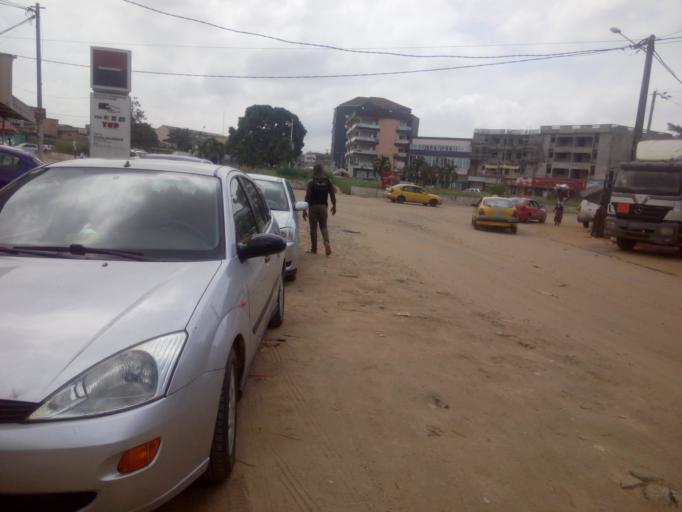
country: CI
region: Lagunes
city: Abidjan
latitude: 5.3642
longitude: -3.9606
